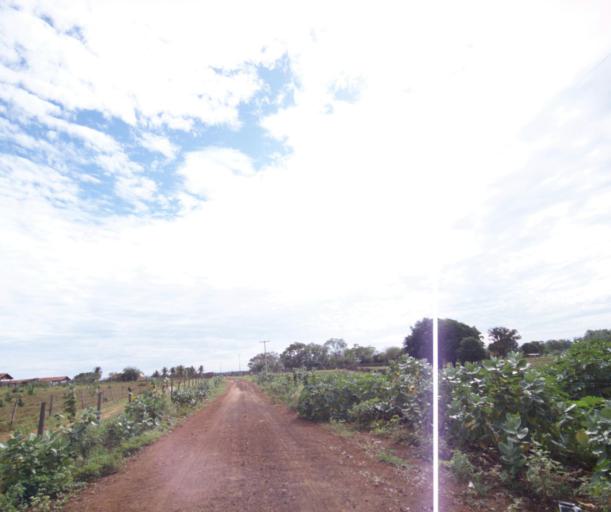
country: BR
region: Bahia
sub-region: Carinhanha
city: Carinhanha
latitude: -14.2391
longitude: -44.4102
